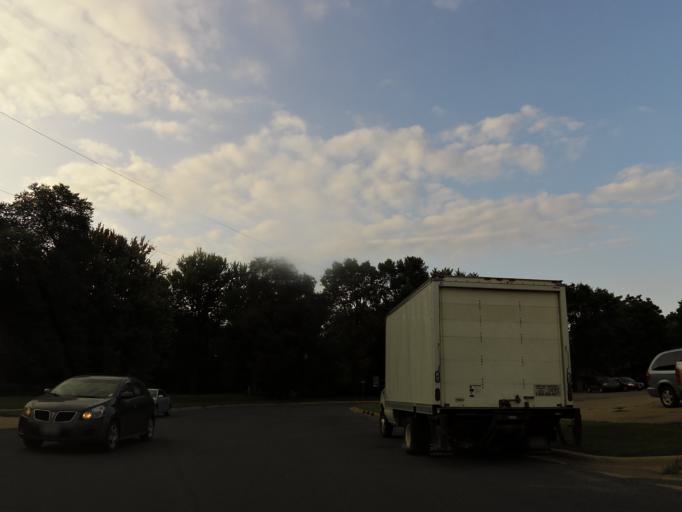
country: US
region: Minnesota
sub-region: Dakota County
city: Farmington
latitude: 44.6434
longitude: -93.1435
